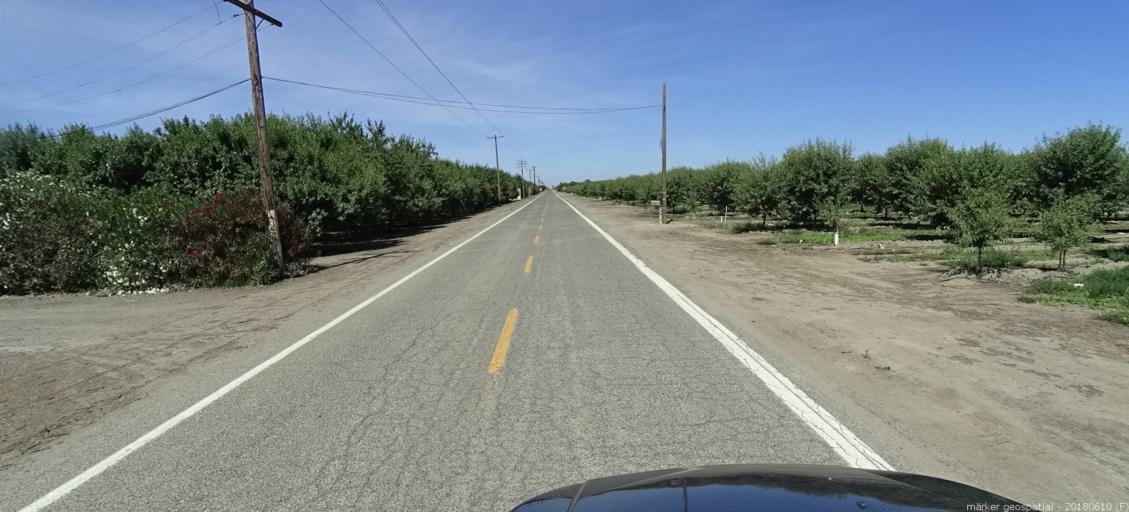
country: US
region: California
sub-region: Madera County
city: Chowchilla
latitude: 37.0400
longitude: -120.2878
